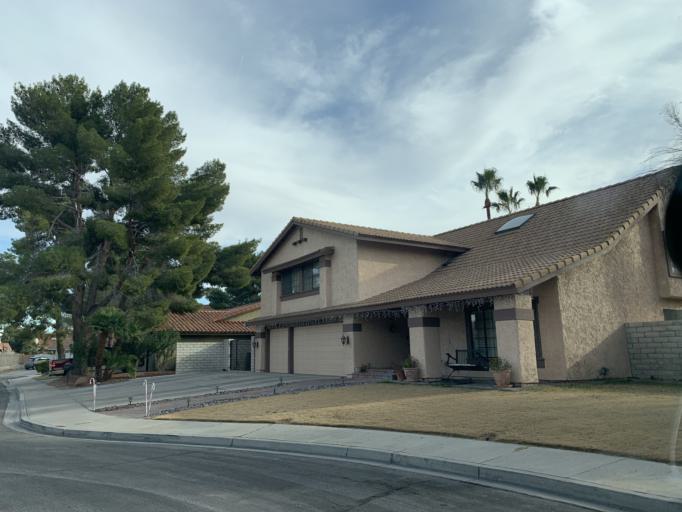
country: US
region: Nevada
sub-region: Clark County
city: Las Vegas
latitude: 36.1483
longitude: -115.1764
